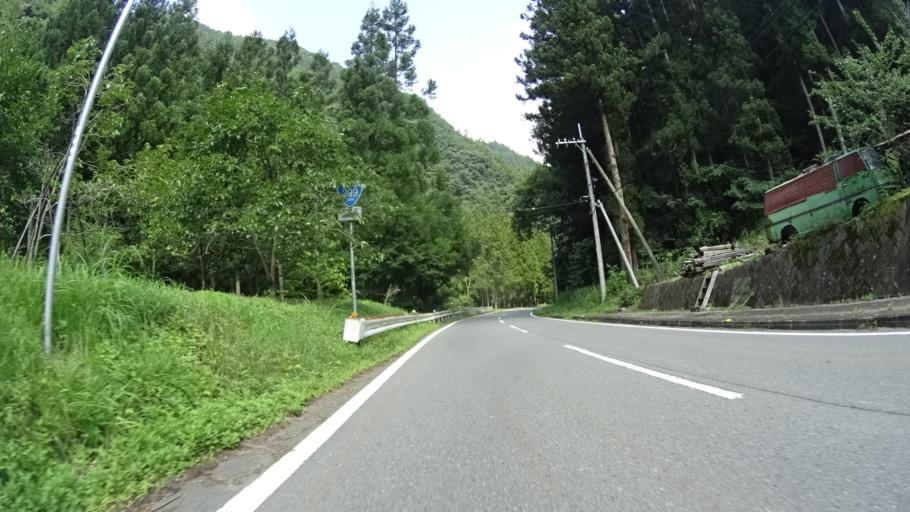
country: JP
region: Gunma
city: Tomioka
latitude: 36.0749
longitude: 138.8269
